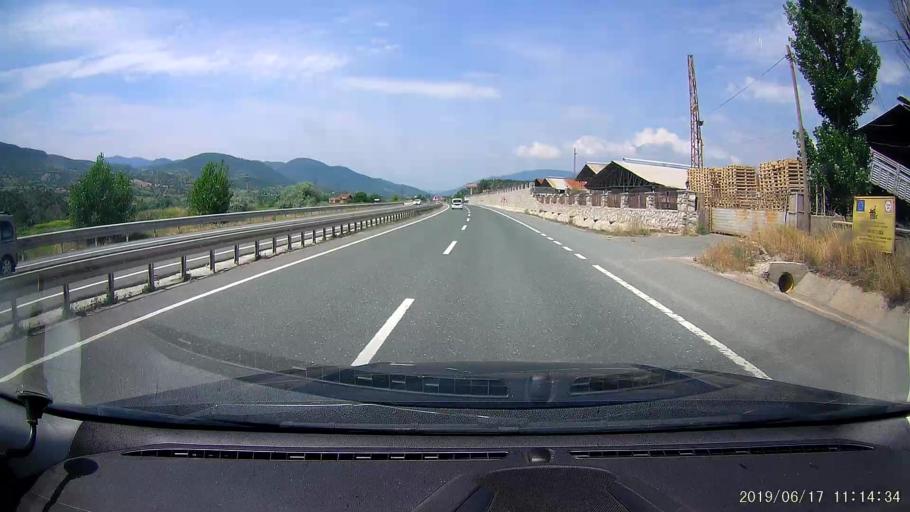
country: TR
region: Kastamonu
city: Tosya
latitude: 40.9573
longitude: 33.9443
